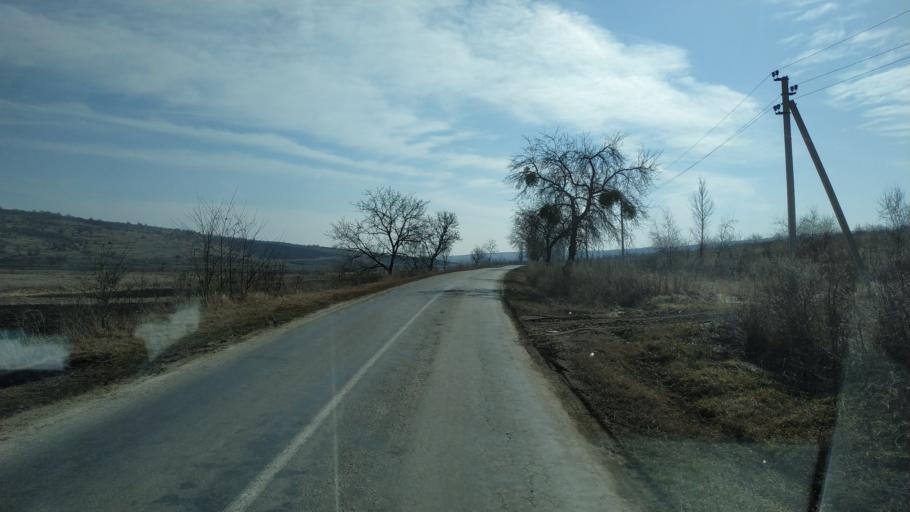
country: MD
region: Nisporeni
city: Nisporeni
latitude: 47.1306
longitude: 28.1210
